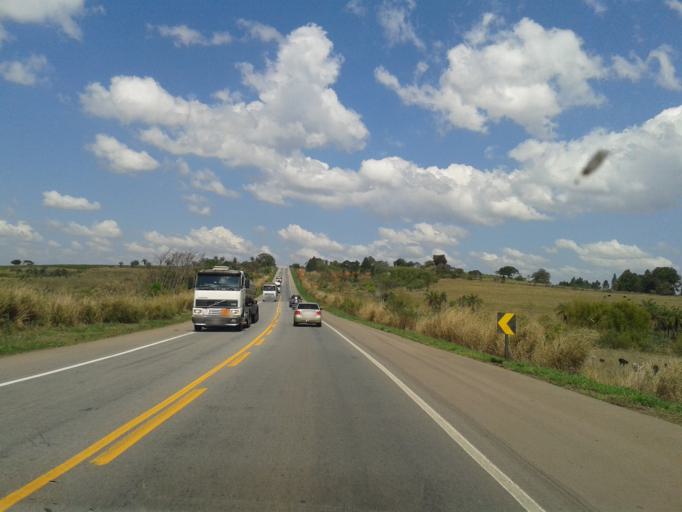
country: BR
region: Minas Gerais
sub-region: Campos Altos
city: Campos Altos
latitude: -19.6916
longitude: -46.0376
